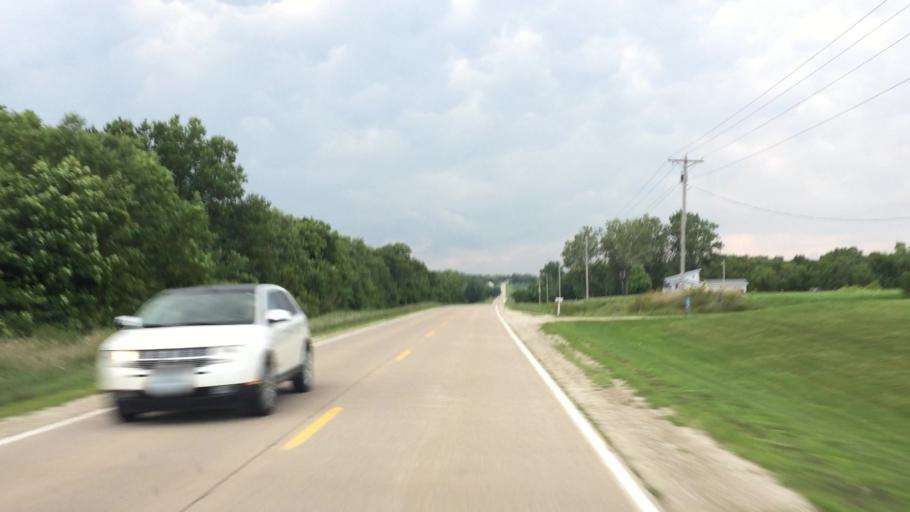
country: US
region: Iowa
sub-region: Lee County
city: Fort Madison
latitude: 40.7114
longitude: -91.3300
